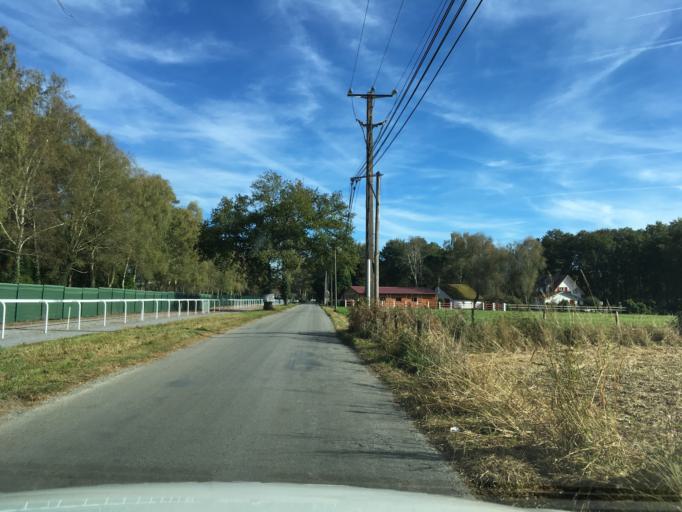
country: FR
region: Aquitaine
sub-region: Departement des Pyrenees-Atlantiques
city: Montardon
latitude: 43.3442
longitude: -0.3744
